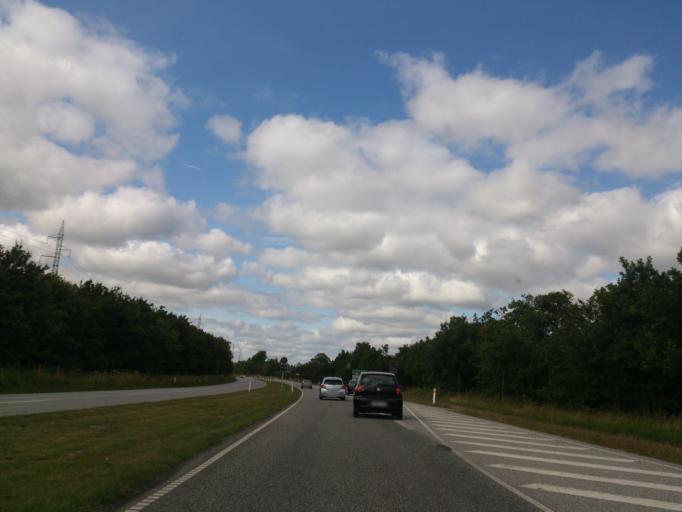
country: DK
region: South Denmark
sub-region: Aabenraa Kommune
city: Krusa
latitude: 54.8582
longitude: 9.4035
